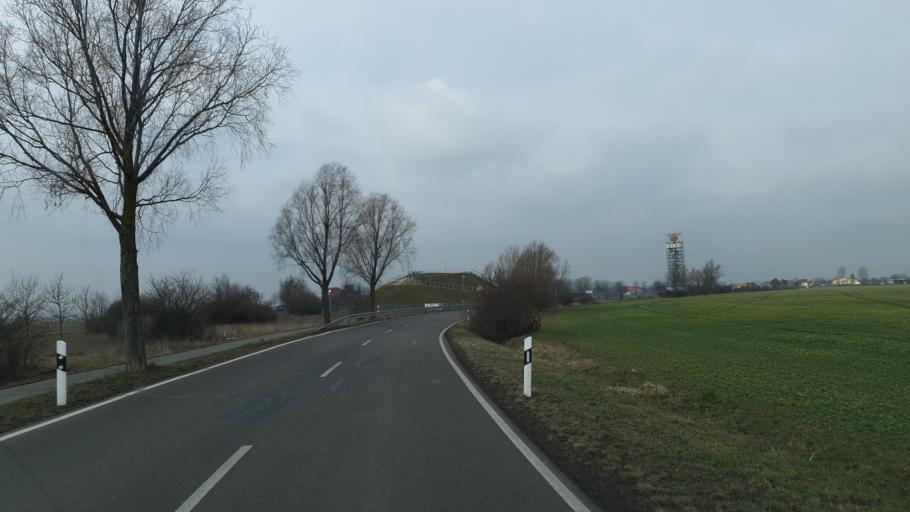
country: DE
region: Saxony
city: Zwochau
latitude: 51.4359
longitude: 12.2473
